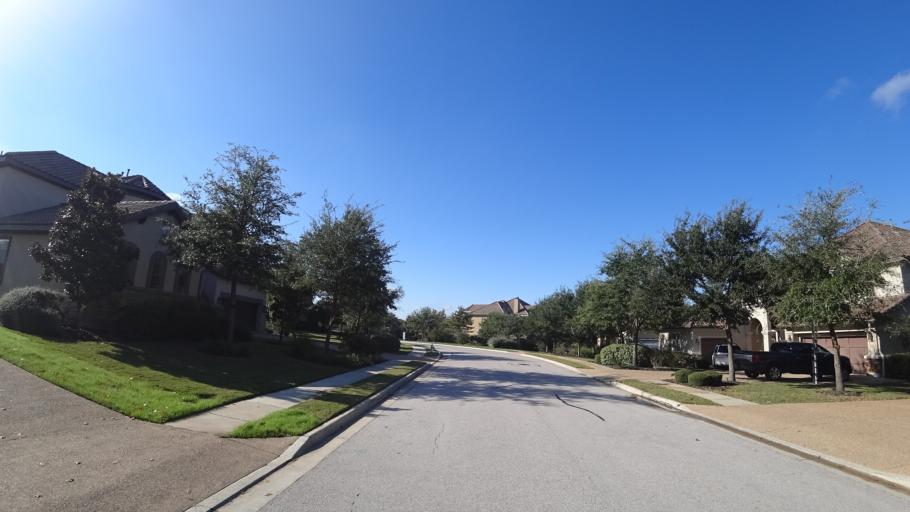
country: US
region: Texas
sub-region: Travis County
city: Bee Cave
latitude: 30.3513
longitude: -97.8955
